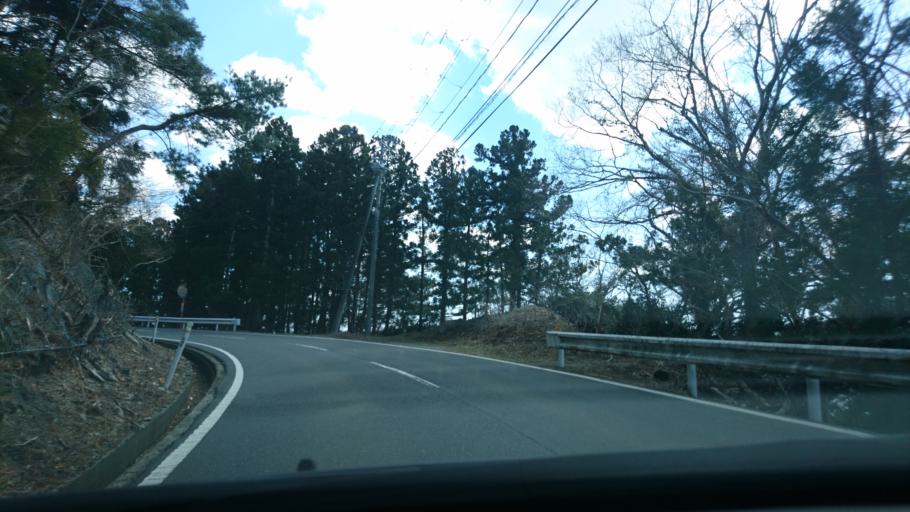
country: JP
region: Miyagi
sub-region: Oshika Gun
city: Onagawa Cho
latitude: 38.4704
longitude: 141.4860
